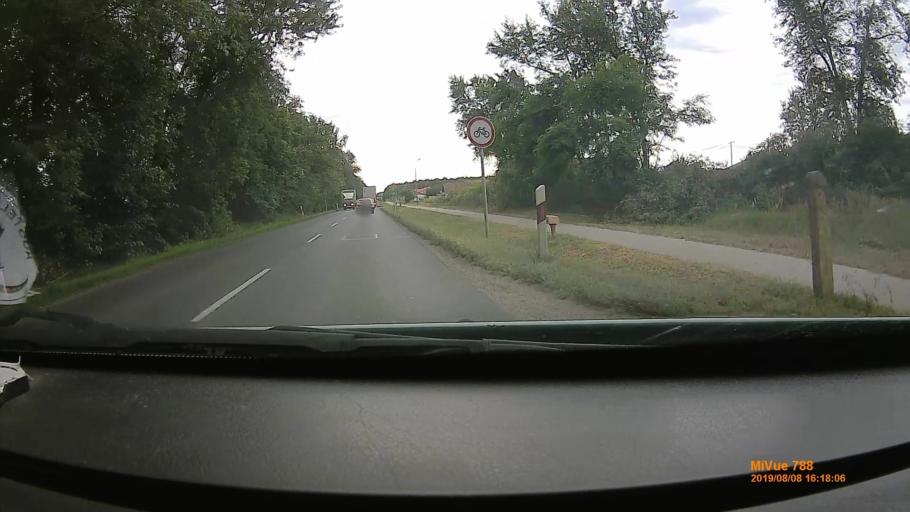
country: HU
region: Szabolcs-Szatmar-Bereg
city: Mateszalka
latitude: 47.9644
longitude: 22.2859
